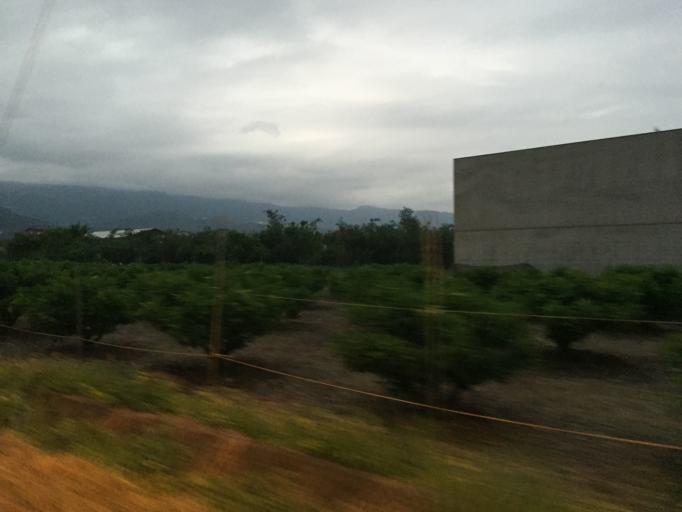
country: TW
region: Taiwan
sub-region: Yilan
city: Yilan
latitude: 24.7613
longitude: 121.7366
